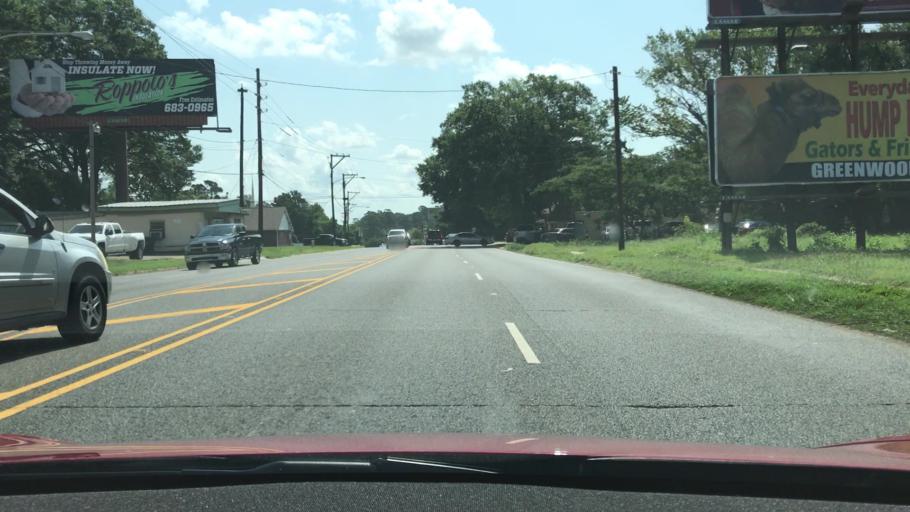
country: US
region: Louisiana
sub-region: Bossier Parish
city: Bossier City
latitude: 32.4420
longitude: -93.7454
